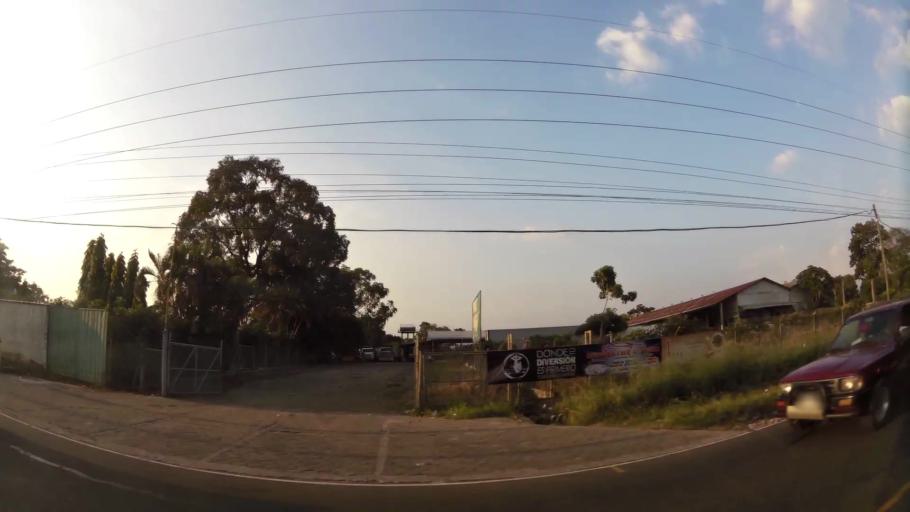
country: GT
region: Retalhuleu
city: San Sebastian
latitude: 14.5495
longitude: -91.6608
